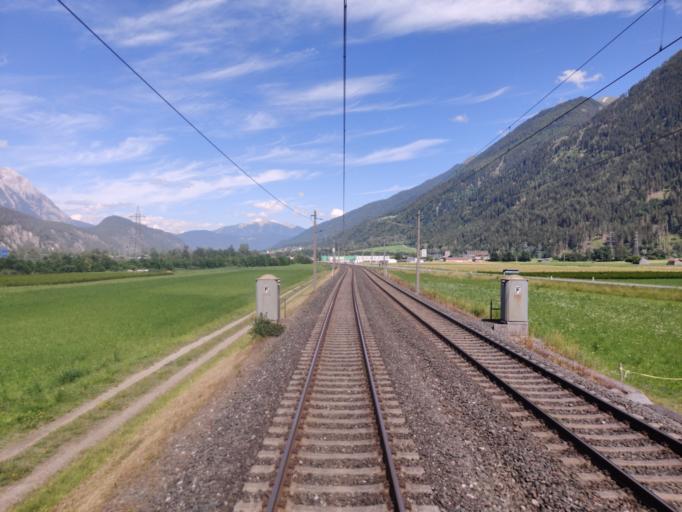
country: AT
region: Tyrol
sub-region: Politischer Bezirk Imst
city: Motz
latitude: 47.2714
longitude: 10.9456
